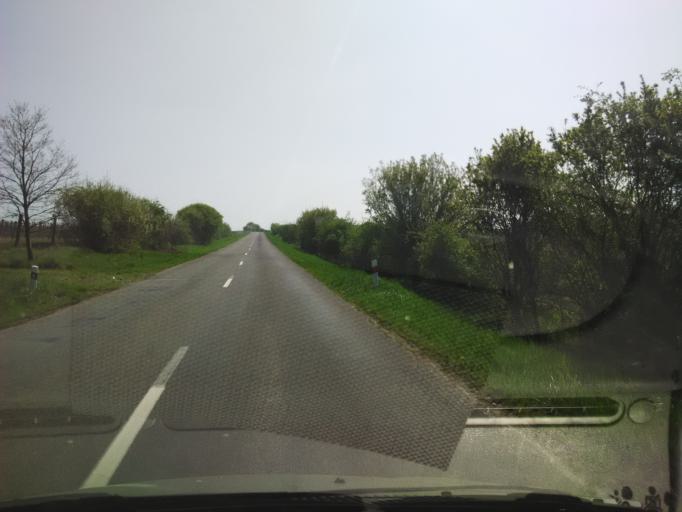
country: SK
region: Nitriansky
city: Levice
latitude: 48.2879
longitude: 18.6793
